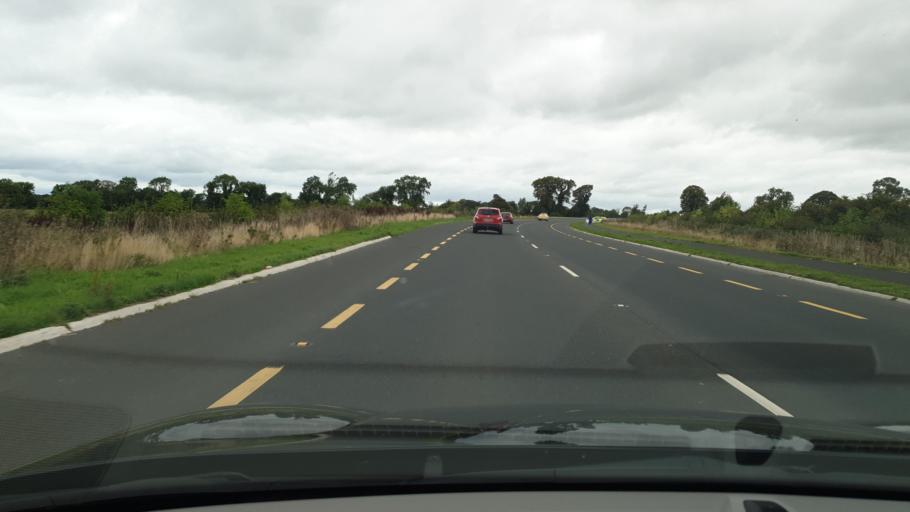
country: IE
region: Leinster
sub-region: Kildare
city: Sallins
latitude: 53.2544
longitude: -6.6808
